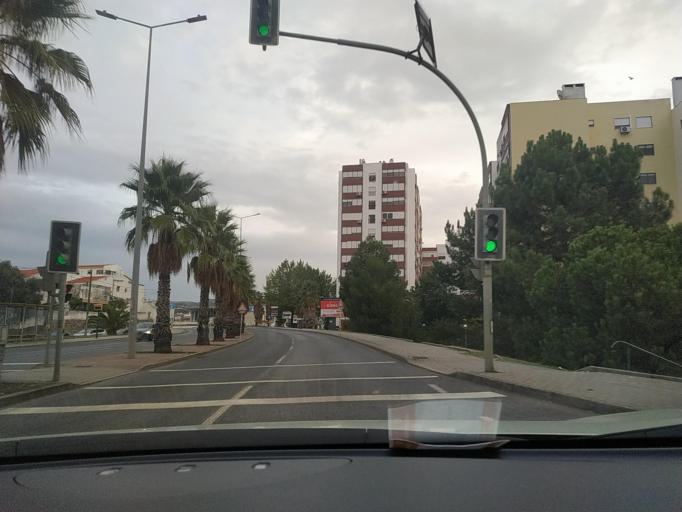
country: PT
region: Lisbon
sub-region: Loures
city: Loures
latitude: 38.8420
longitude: -9.1630
